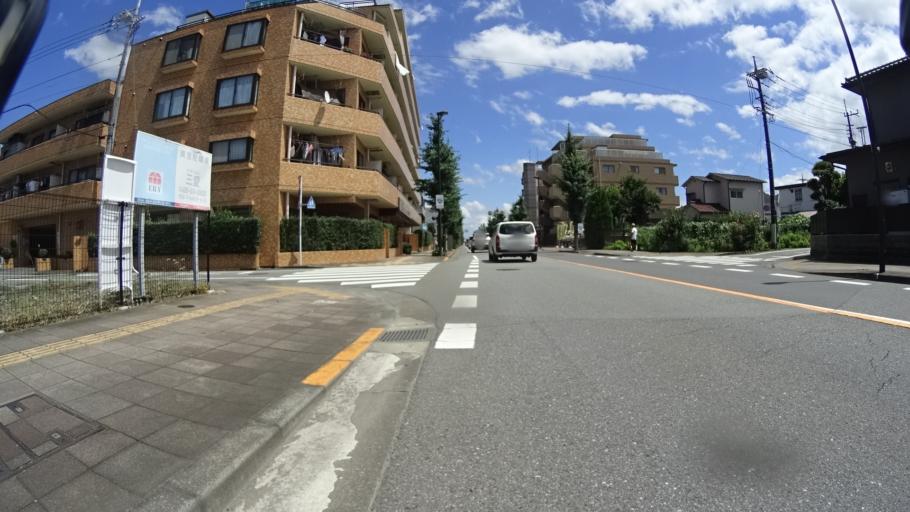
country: JP
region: Tokyo
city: Ome
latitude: 35.7848
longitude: 139.2808
